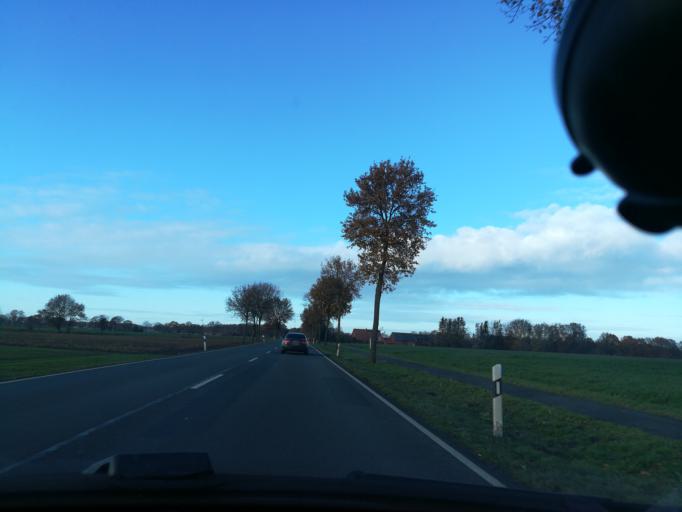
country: DE
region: Lower Saxony
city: Uchte
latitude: 52.4608
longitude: 8.9152
